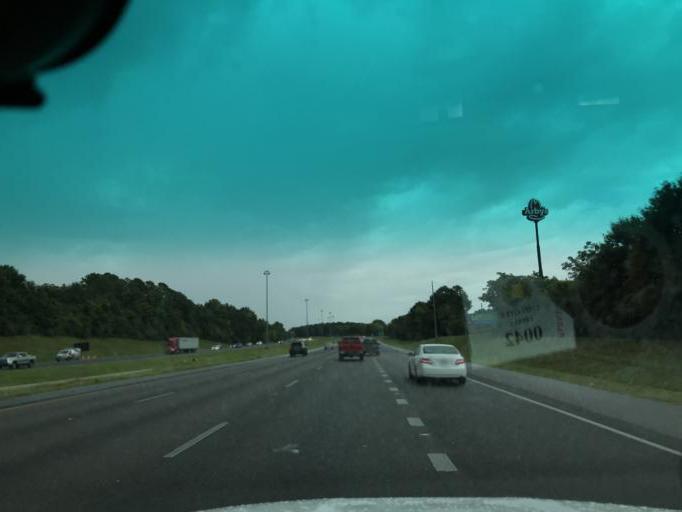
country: US
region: Alabama
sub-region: Montgomery County
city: Montgomery
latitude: 32.3646
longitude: -86.2664
